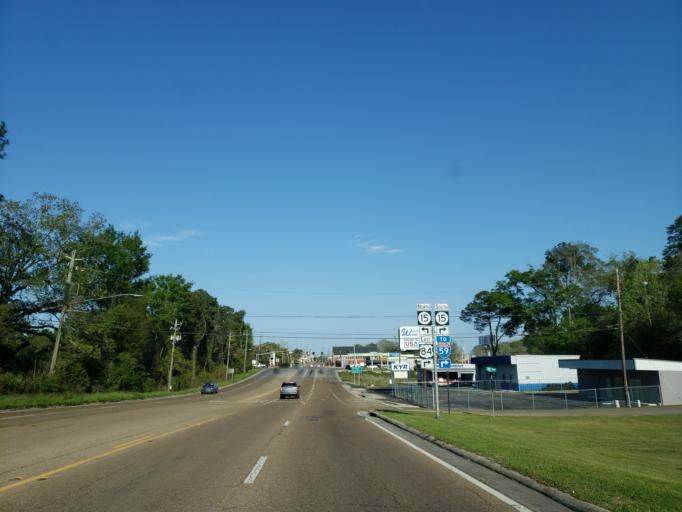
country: US
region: Mississippi
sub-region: Jones County
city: Laurel
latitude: 31.6944
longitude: -89.1492
